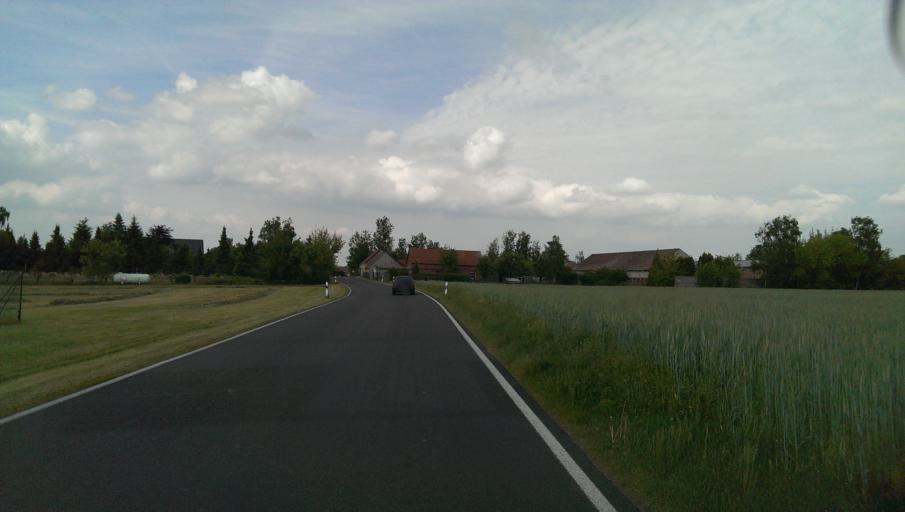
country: DE
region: Brandenburg
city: Niemegk
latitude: 52.1247
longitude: 12.7052
